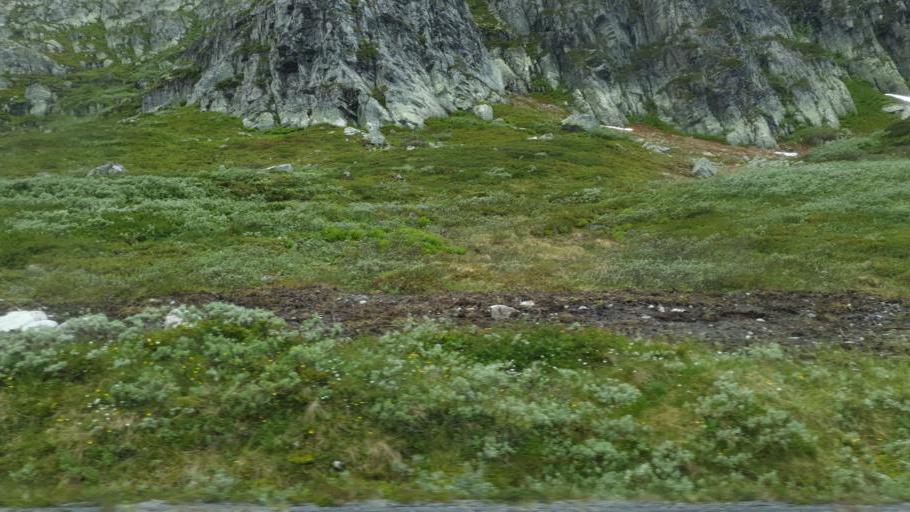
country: NO
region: Oppland
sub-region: Vestre Slidre
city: Slidre
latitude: 61.3088
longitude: 8.8068
